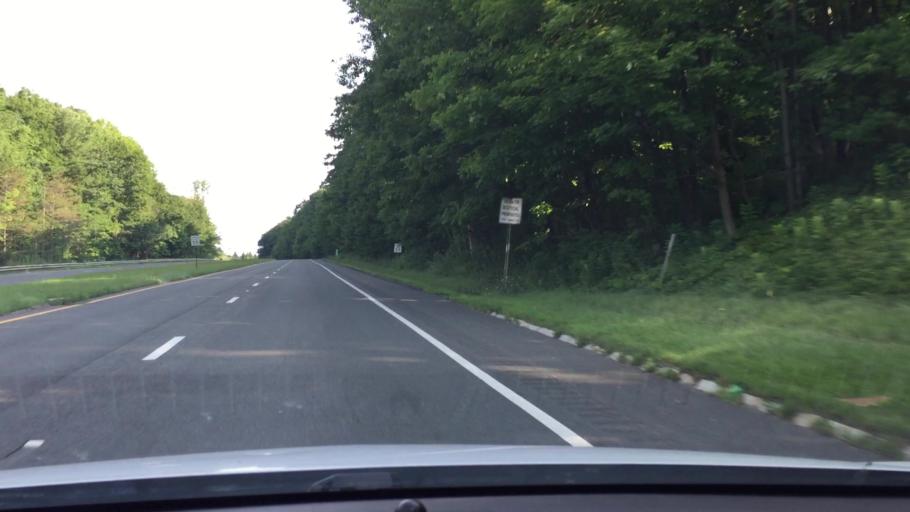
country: US
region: Massachusetts
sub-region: Berkshire County
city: Lenox
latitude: 42.3627
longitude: -73.2752
